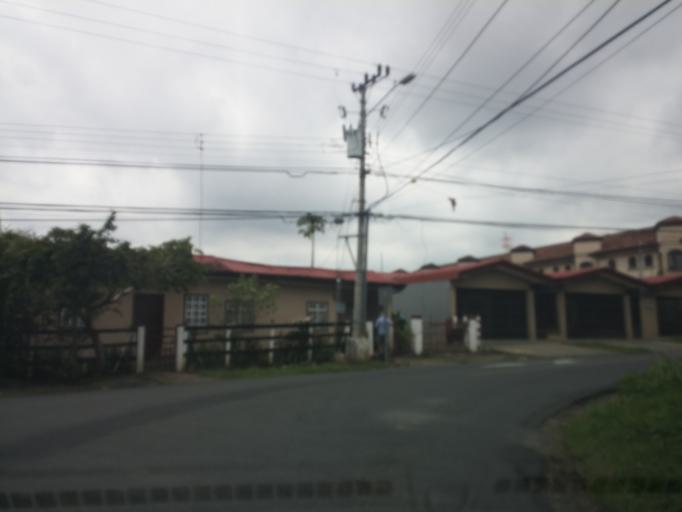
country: CR
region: Heredia
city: Llorente
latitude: 10.0060
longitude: -84.1496
